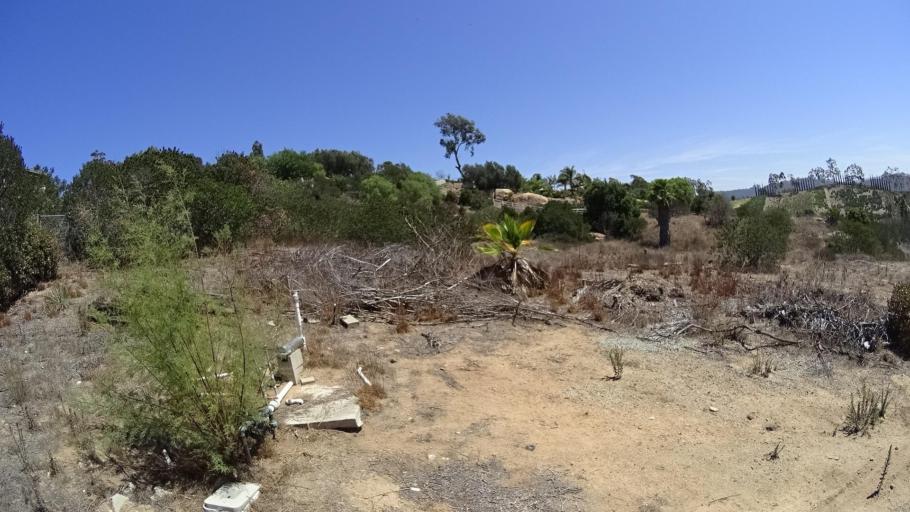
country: US
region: California
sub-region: San Diego County
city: Bonsall
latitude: 33.3286
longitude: -117.1741
